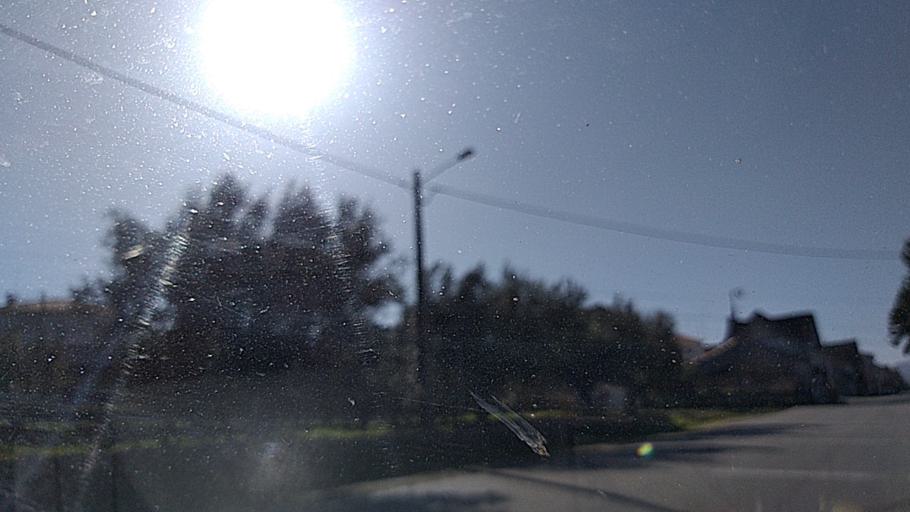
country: PT
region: Guarda
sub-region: Celorico da Beira
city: Celorico da Beira
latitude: 40.6674
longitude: -7.3811
